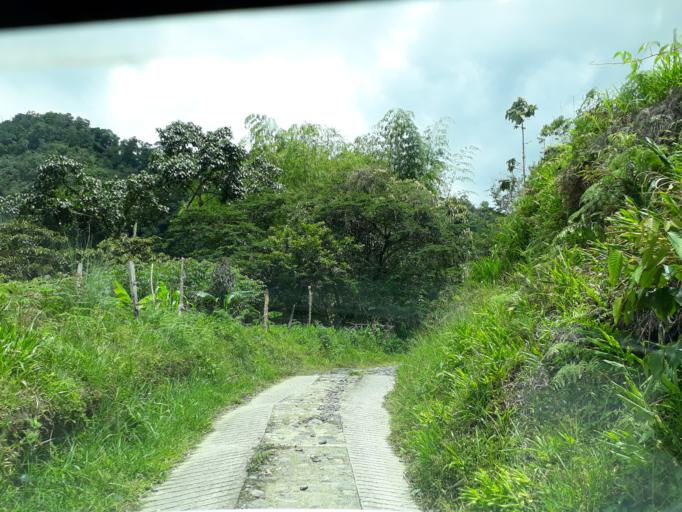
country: CO
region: Cundinamarca
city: Topaipi
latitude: 5.3252
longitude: -74.2156
